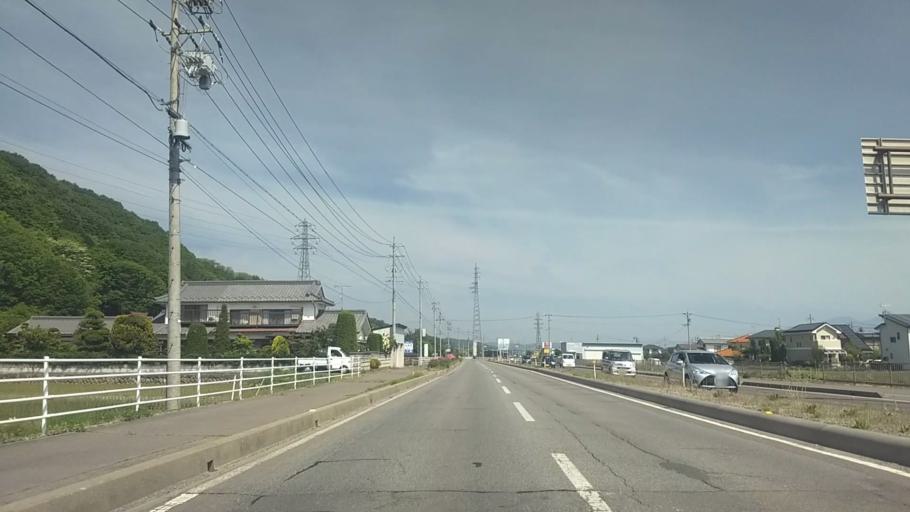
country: JP
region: Nagano
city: Saku
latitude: 36.1986
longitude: 138.4726
